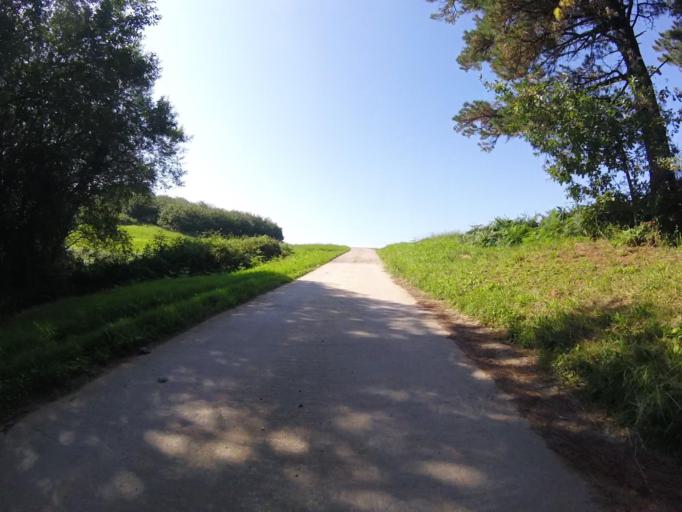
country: ES
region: Basque Country
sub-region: Provincia de Guipuzcoa
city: Astigarraga
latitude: 43.2718
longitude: -1.9244
